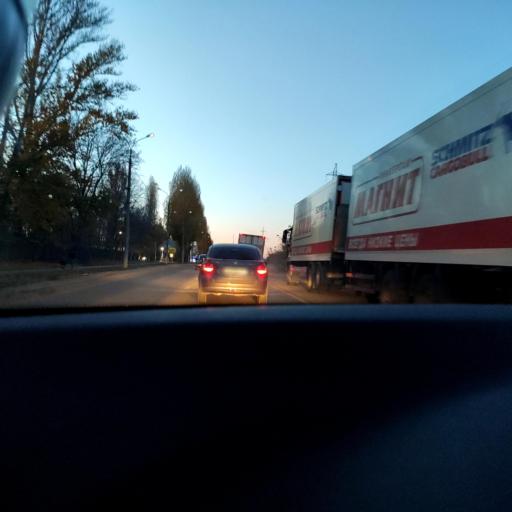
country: RU
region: Samara
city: Petra-Dubrava
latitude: 53.3046
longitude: 50.2810
